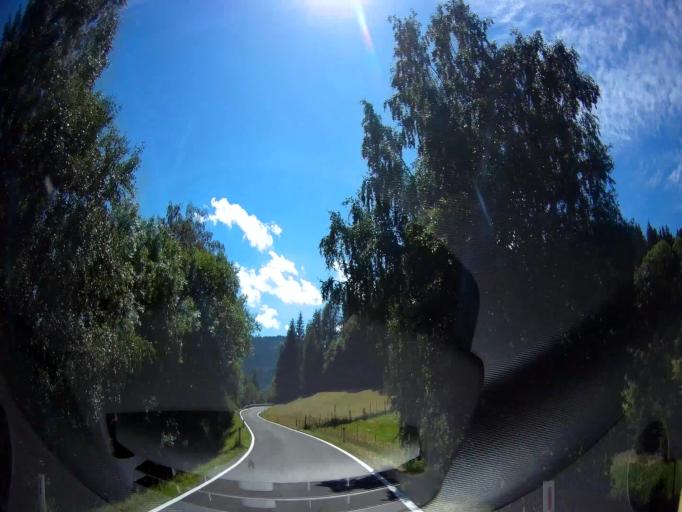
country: AT
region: Carinthia
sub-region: Politischer Bezirk Sankt Veit an der Glan
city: Glodnitz
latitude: 46.9162
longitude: 14.0808
